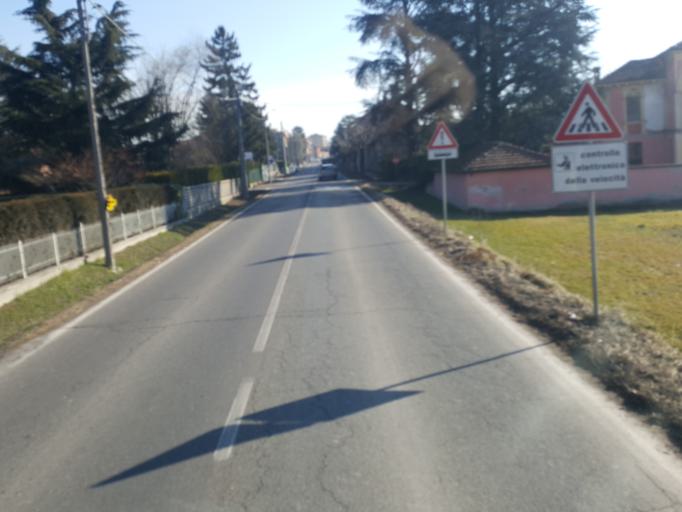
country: IT
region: Piedmont
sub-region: Provincia di Alessandria
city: Viguzzolo
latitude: 44.9074
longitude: 8.9104
